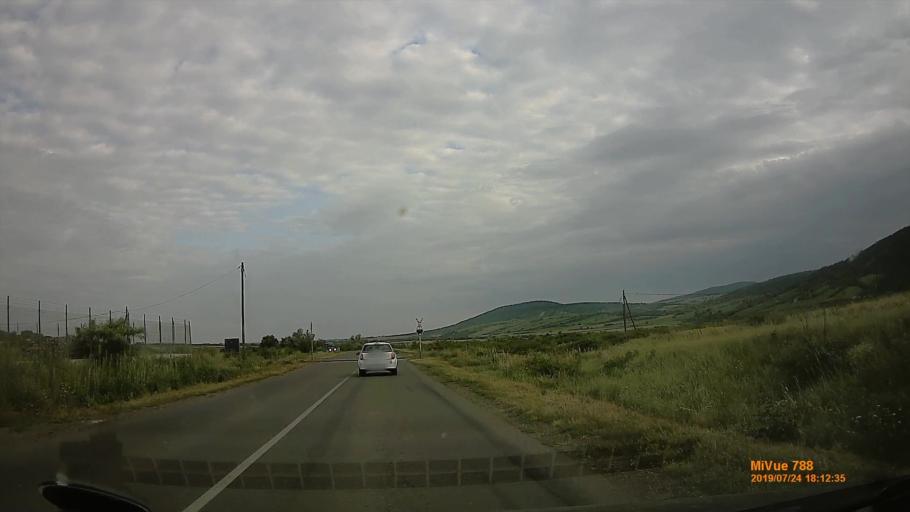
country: HU
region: Borsod-Abauj-Zemplen
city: Tallya
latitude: 48.2366
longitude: 21.2127
